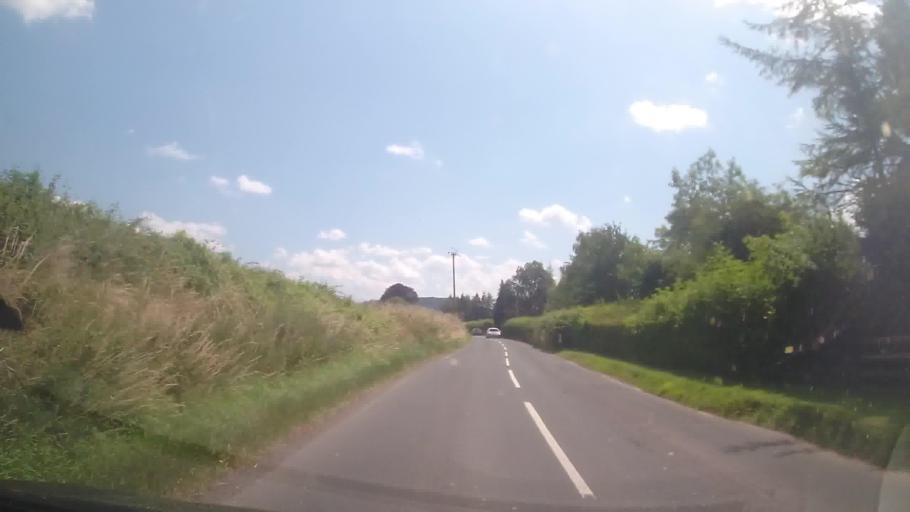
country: GB
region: England
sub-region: Herefordshire
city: Brockhampton
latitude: 52.0118
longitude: -2.6217
